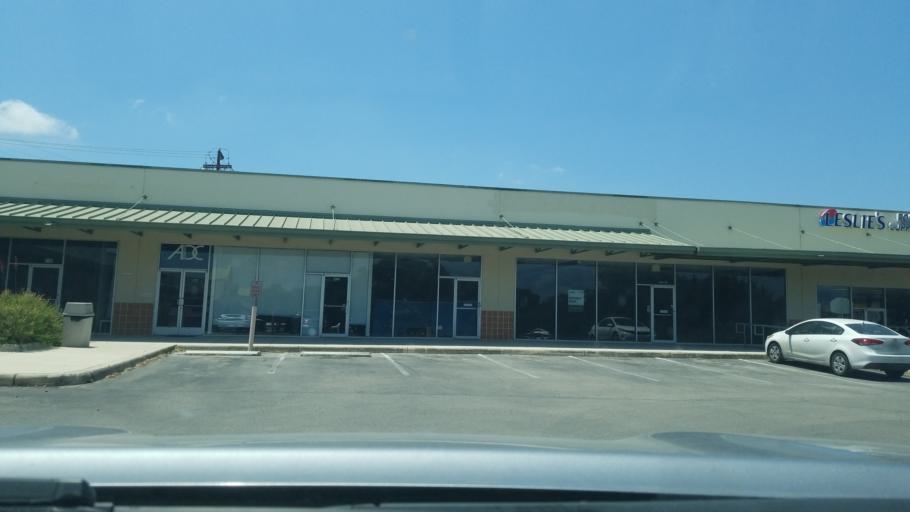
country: US
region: Texas
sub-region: Comal County
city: Bulverde
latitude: 29.7965
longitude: -98.4272
